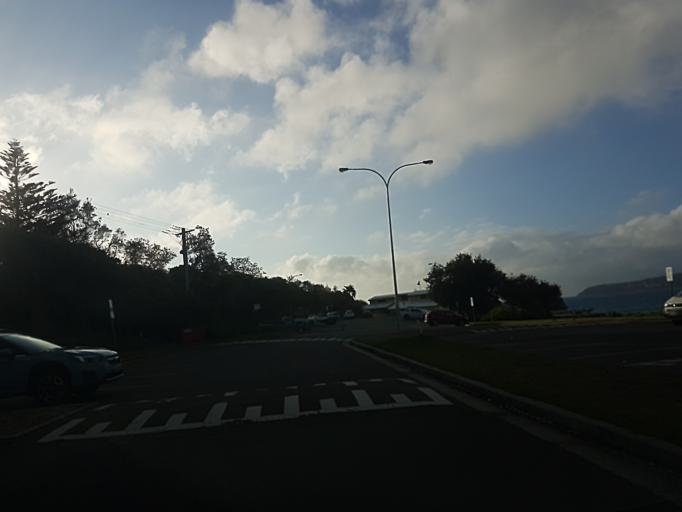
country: AU
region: New South Wales
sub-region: Warringah
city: North Curl Curl
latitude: -33.7653
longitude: 151.2987
